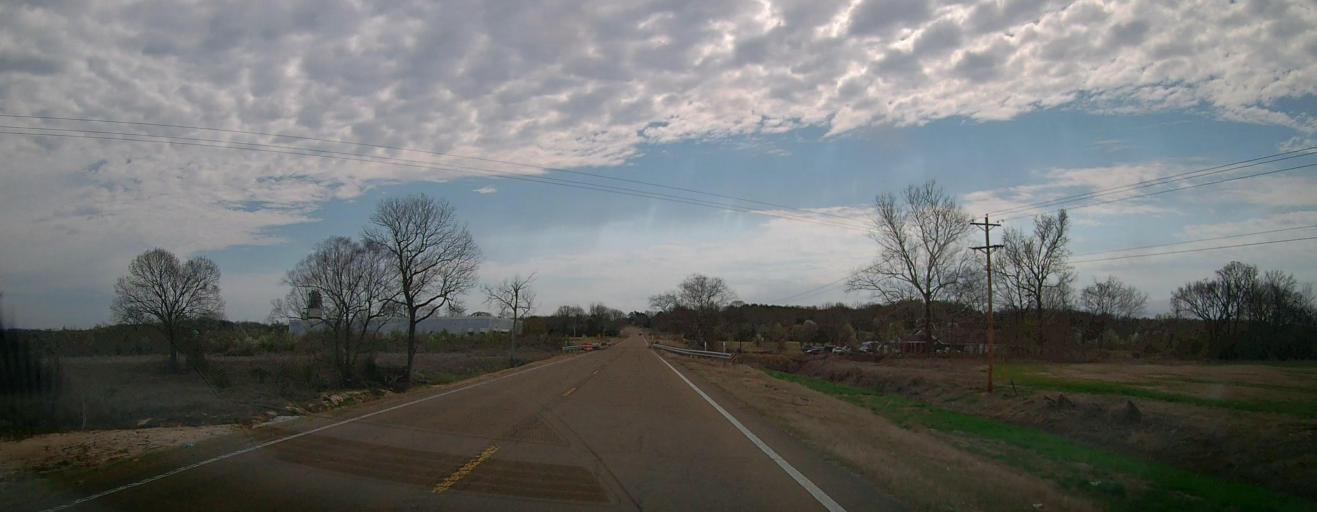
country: US
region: Mississippi
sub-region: Marshall County
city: Byhalia
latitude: 34.8659
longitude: -89.6640
